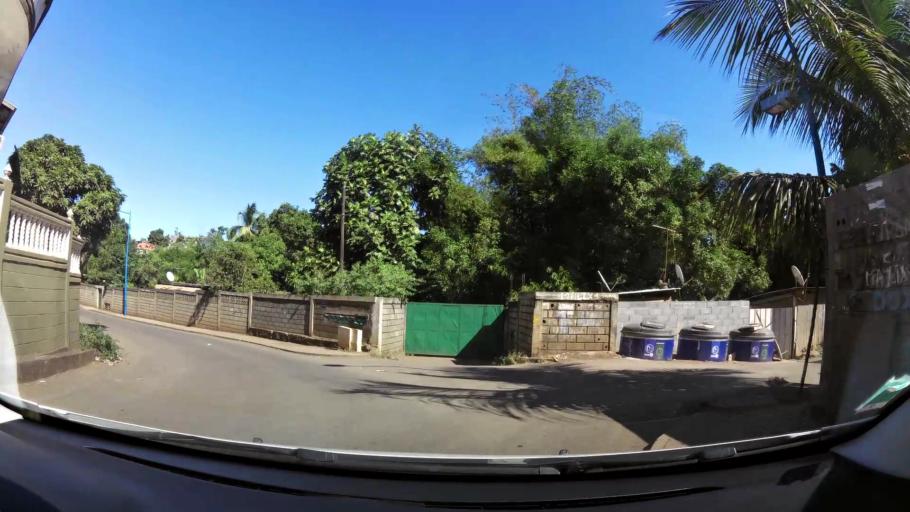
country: YT
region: Mamoudzou
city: Mamoudzou
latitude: -12.7871
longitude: 45.2170
